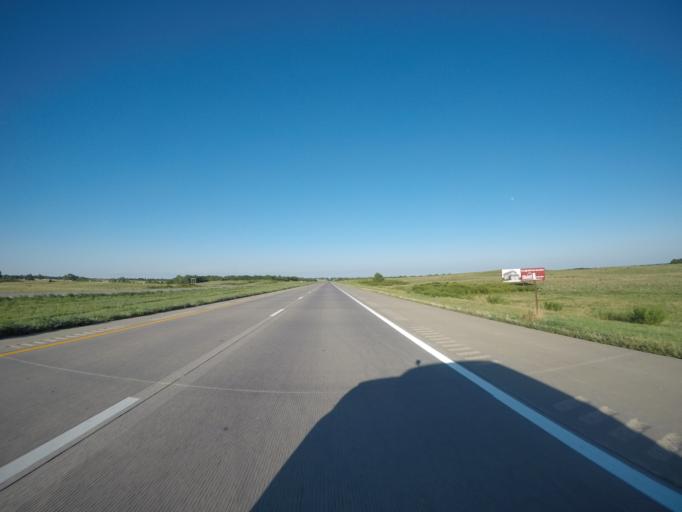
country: US
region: Kansas
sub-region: Dickinson County
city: Solomon
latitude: 38.9295
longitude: -97.2948
